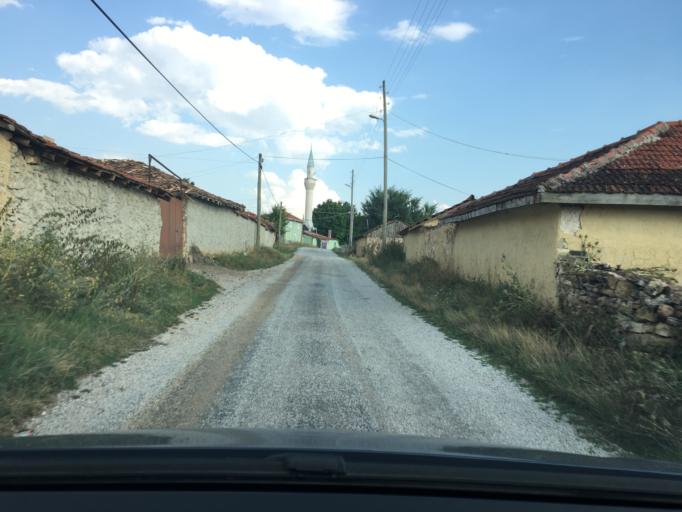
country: TR
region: Eskisehir
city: Kirka
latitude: 39.2774
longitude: 30.6759
